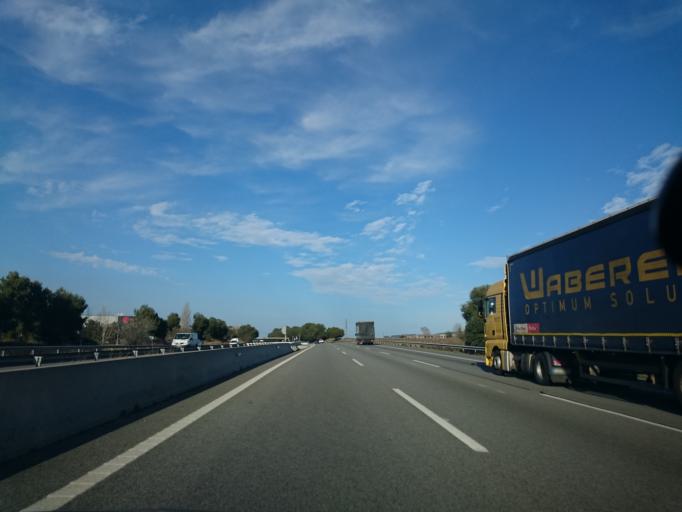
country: ES
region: Catalonia
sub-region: Provincia de Barcelona
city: La Granada
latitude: 41.3720
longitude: 1.7311
